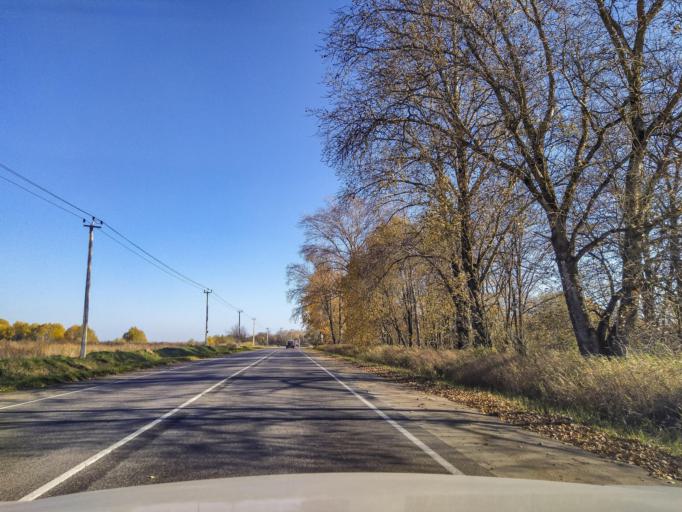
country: RU
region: Leningrad
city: Rozhdestveno
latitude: 59.3466
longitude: 29.9681
